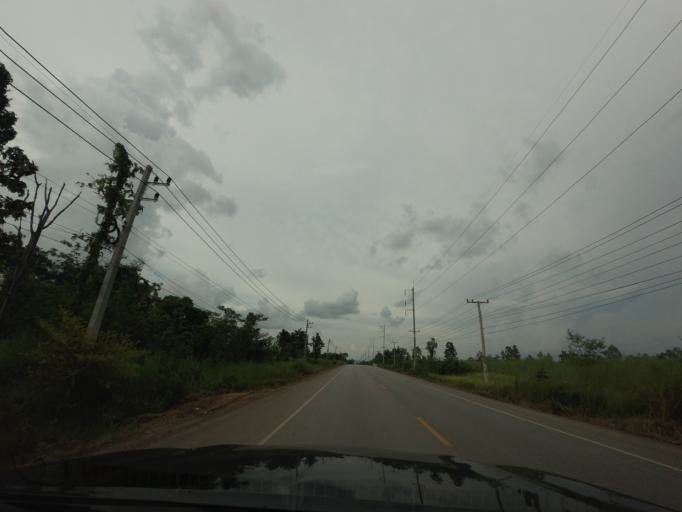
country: TH
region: Changwat Nong Bua Lamphu
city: Nong Bua Lamphu
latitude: 17.1290
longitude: 102.4015
